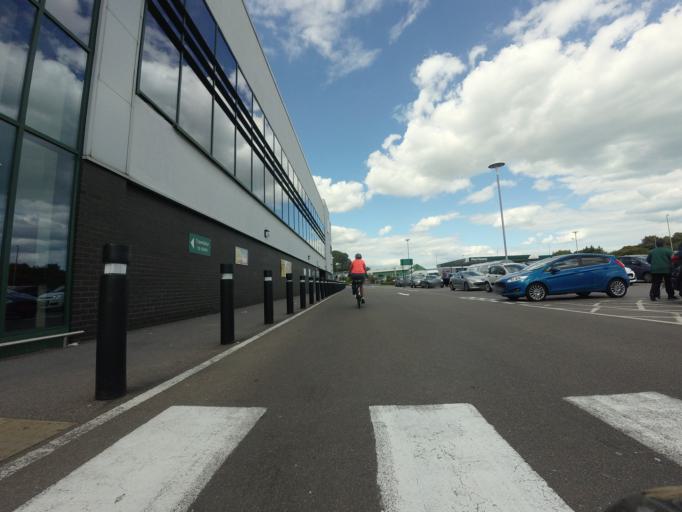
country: GB
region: England
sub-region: East Sussex
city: Eastbourne
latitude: 50.7965
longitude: 0.2854
